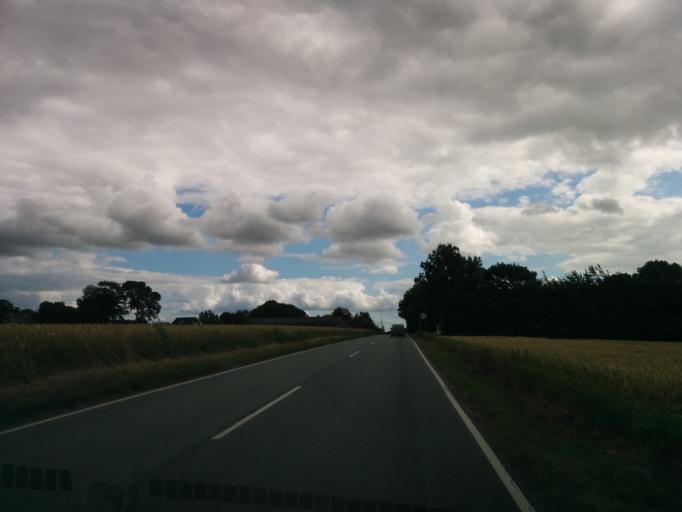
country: DK
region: Central Jutland
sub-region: Arhus Kommune
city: Kolt
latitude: 56.1140
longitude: 10.0701
